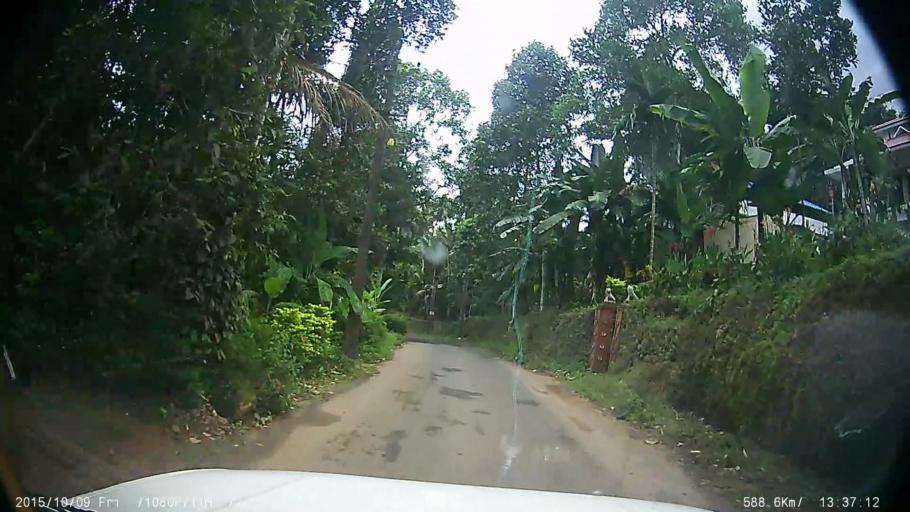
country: IN
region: Kerala
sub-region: Ernakulam
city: Piravam
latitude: 9.8945
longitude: 76.5635
